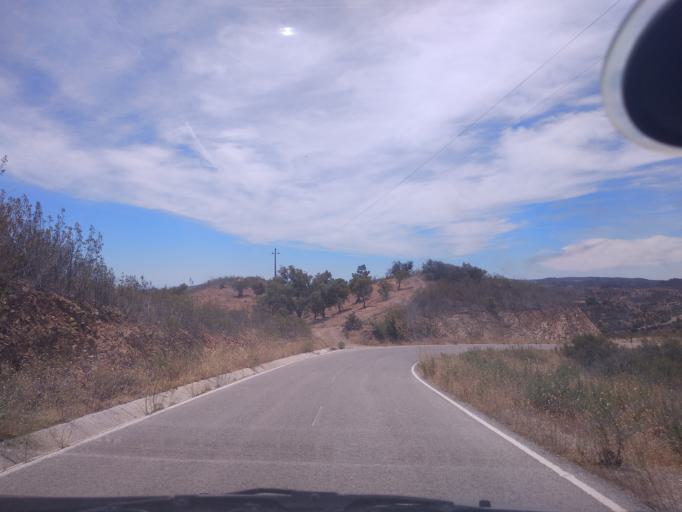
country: PT
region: Faro
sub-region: Sao Bras de Alportel
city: Sao Bras de Alportel
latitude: 37.1880
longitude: -7.7972
